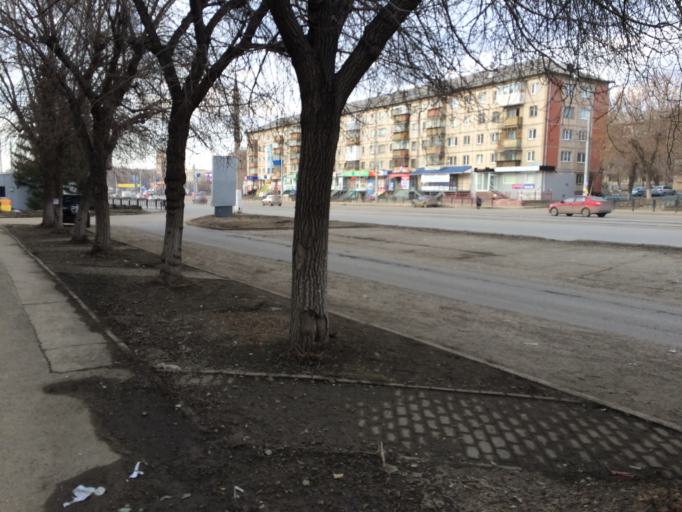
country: RU
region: Chelyabinsk
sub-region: Gorod Magnitogorsk
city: Magnitogorsk
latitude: 53.4002
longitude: 58.9785
